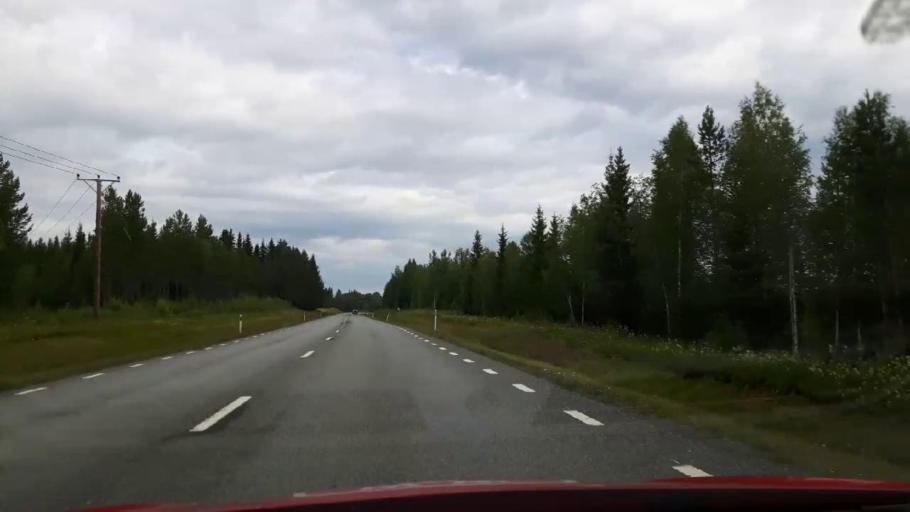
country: SE
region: Jaemtland
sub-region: Stroemsunds Kommun
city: Stroemsund
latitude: 63.6539
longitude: 15.3842
